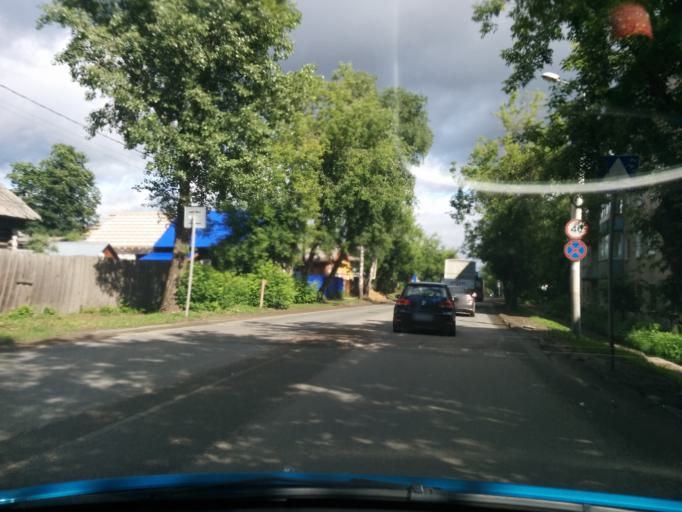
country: RU
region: Perm
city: Kondratovo
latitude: 58.0440
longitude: 56.1007
